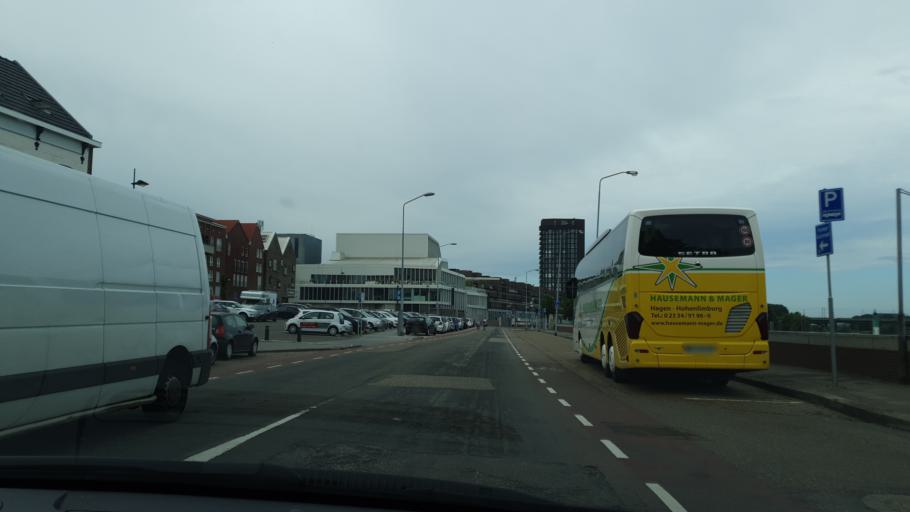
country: NL
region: Limburg
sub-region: Gemeente Venlo
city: Venlo
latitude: 51.3727
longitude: 6.1682
